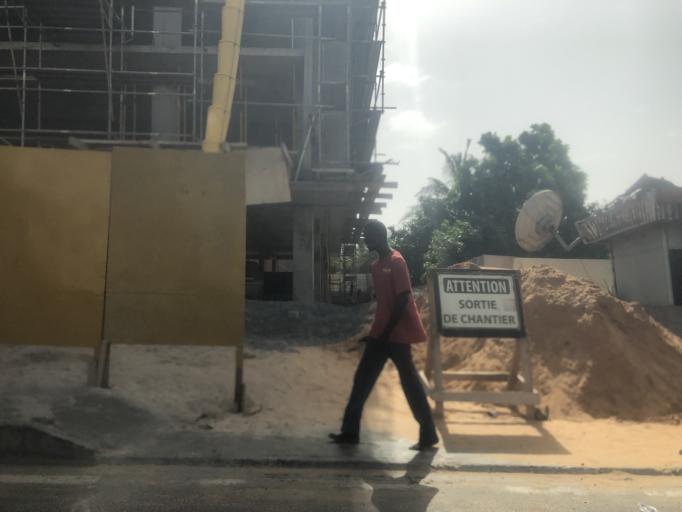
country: SN
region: Dakar
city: Mermoz Boabab
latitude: 14.7424
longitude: -17.5113
